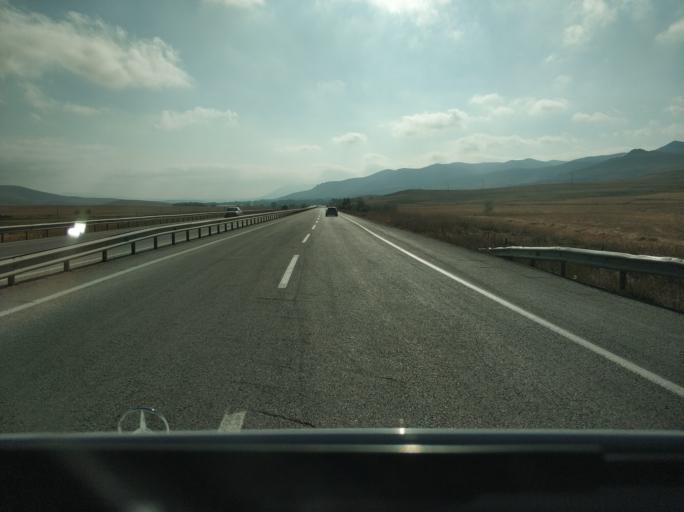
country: TR
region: Sivas
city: Yildizeli
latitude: 39.8351
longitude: 36.4291
